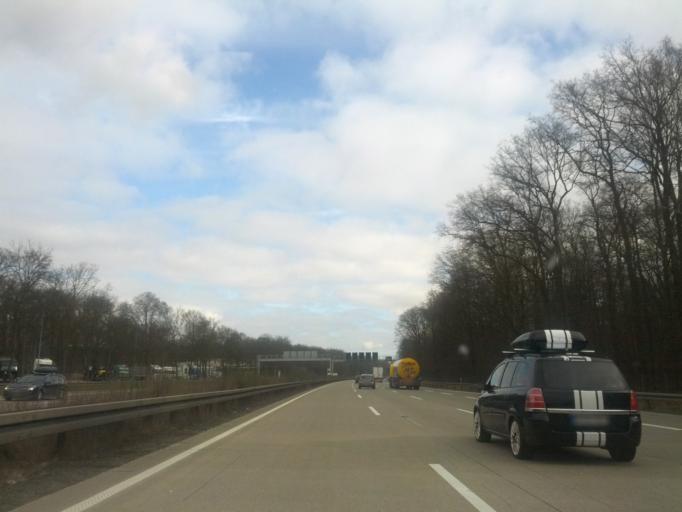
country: DE
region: Lower Saxony
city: Laatzen
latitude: 52.3364
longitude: 9.8649
